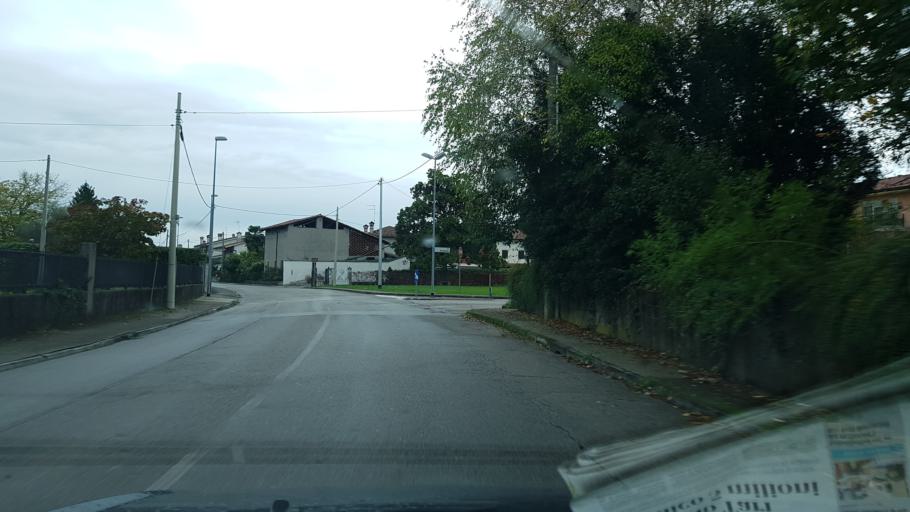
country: IT
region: Friuli Venezia Giulia
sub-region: Provincia di Udine
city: San Valentino
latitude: 45.7929
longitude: 13.4153
